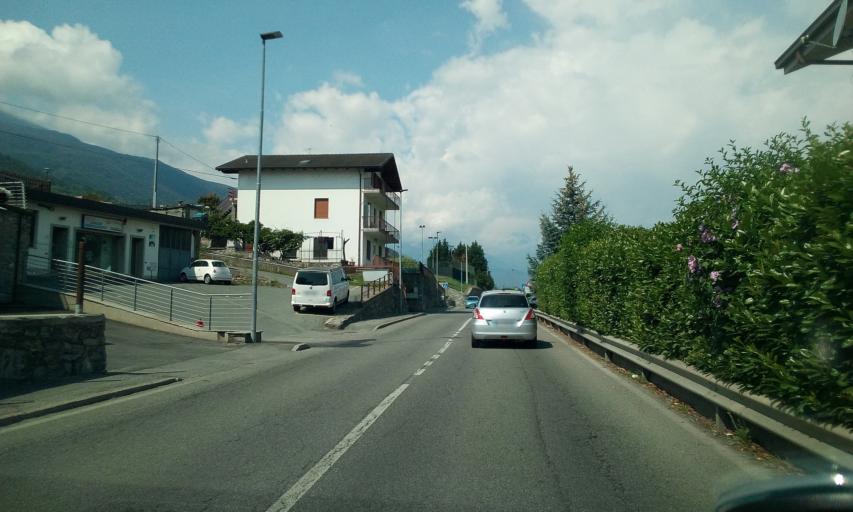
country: IT
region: Aosta Valley
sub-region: Valle d'Aosta
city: Aosta
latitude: 45.7278
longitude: 7.3152
